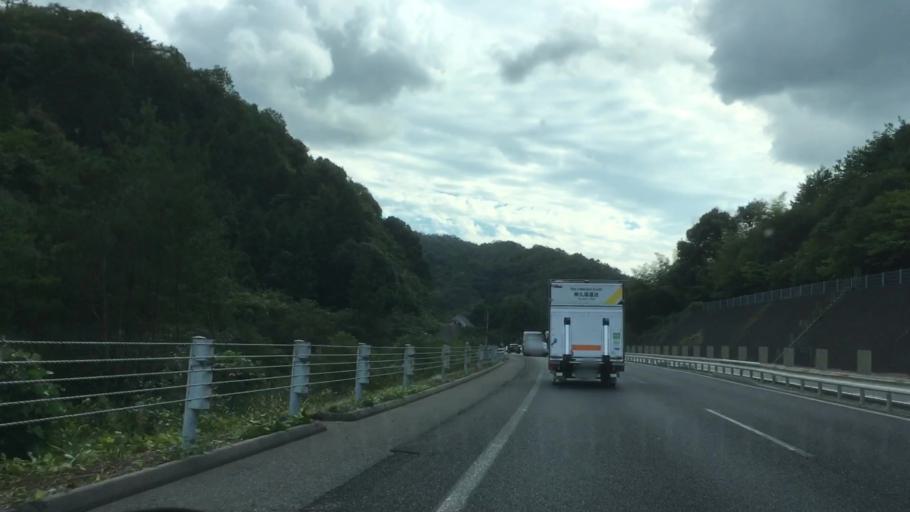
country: JP
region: Yamaguchi
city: Iwakuni
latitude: 34.1263
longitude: 132.1111
